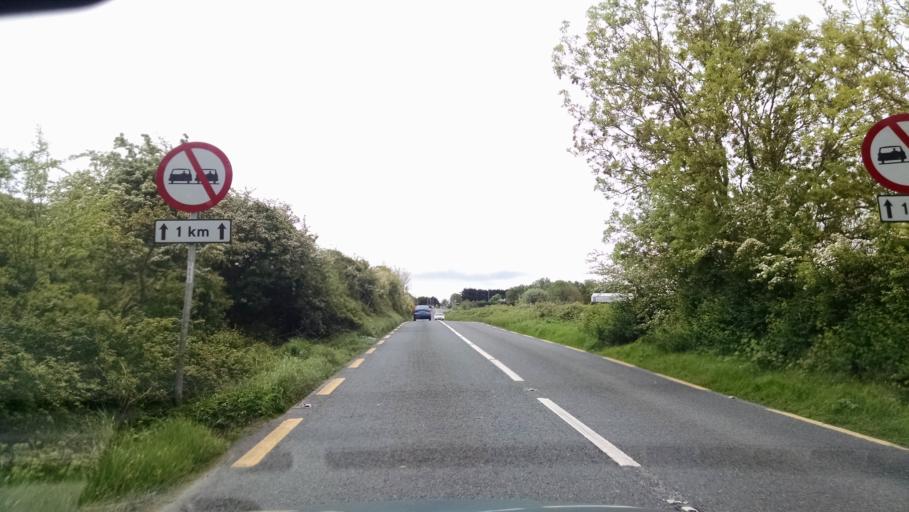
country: IE
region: Connaught
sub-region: County Galway
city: Claregalway
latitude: 53.3812
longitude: -9.0162
